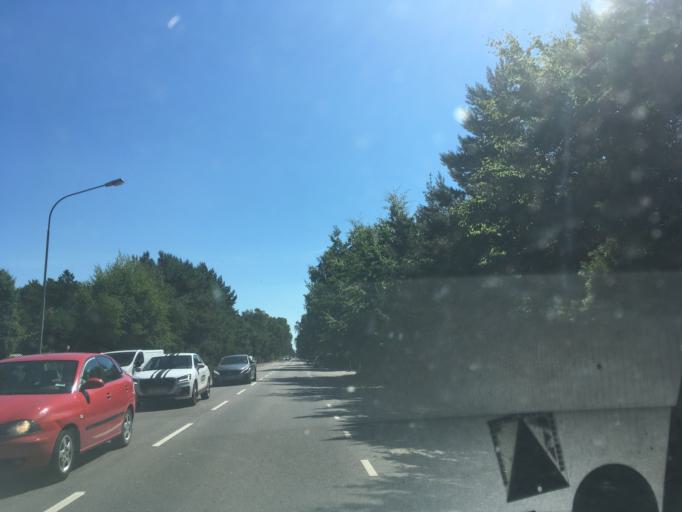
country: SE
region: Skane
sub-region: Vellinge Kommun
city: Hollviken
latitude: 55.4074
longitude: 12.9630
